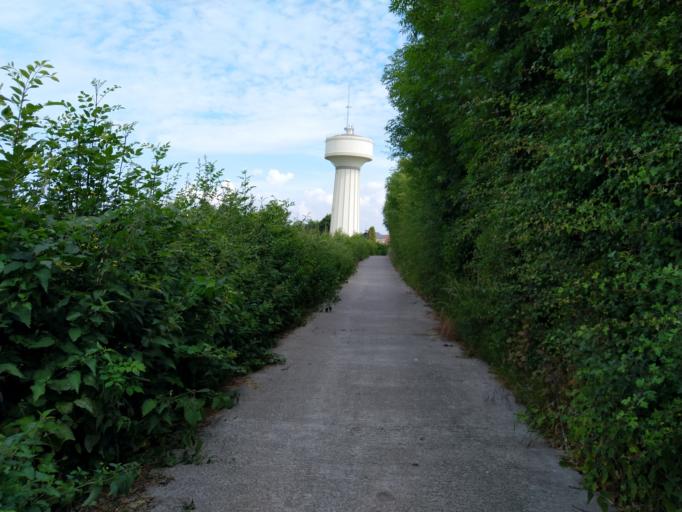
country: FR
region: Nord-Pas-de-Calais
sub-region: Departement du Nord
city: Maubeuge
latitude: 50.2642
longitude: 3.9786
